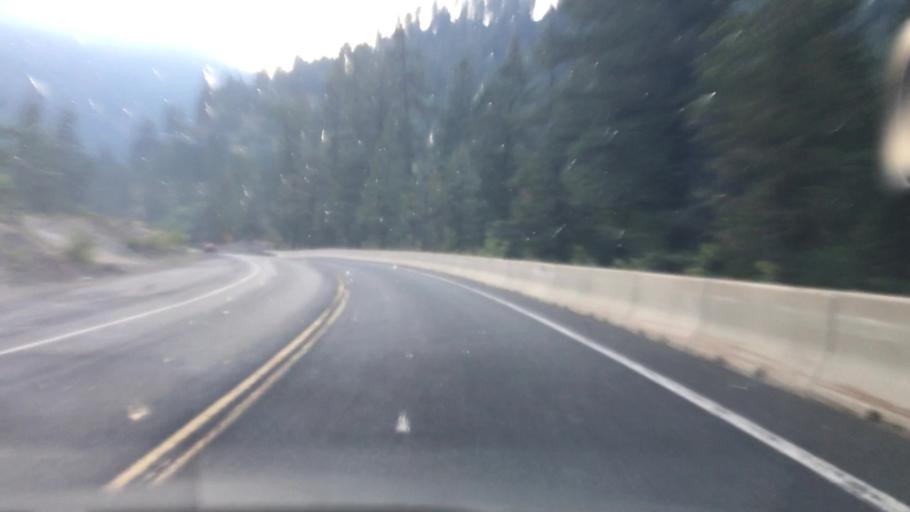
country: US
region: Idaho
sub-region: Valley County
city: McCall
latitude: 45.1468
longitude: -116.2884
